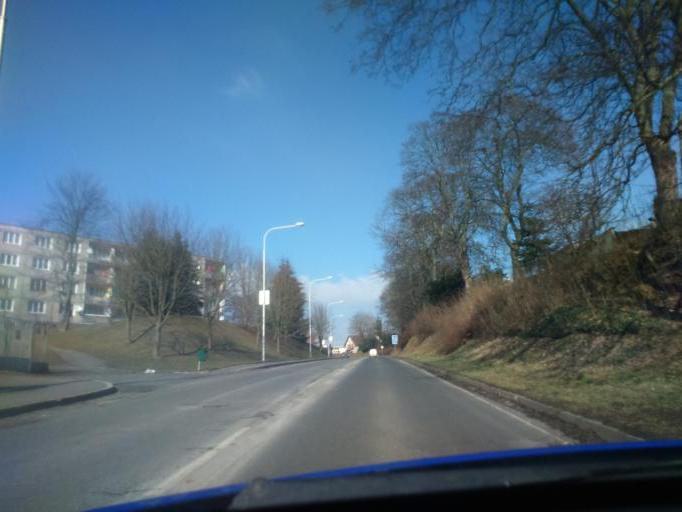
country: CZ
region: Plzensky
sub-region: Okres Domazlice
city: Domazlice
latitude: 49.4446
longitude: 12.9312
